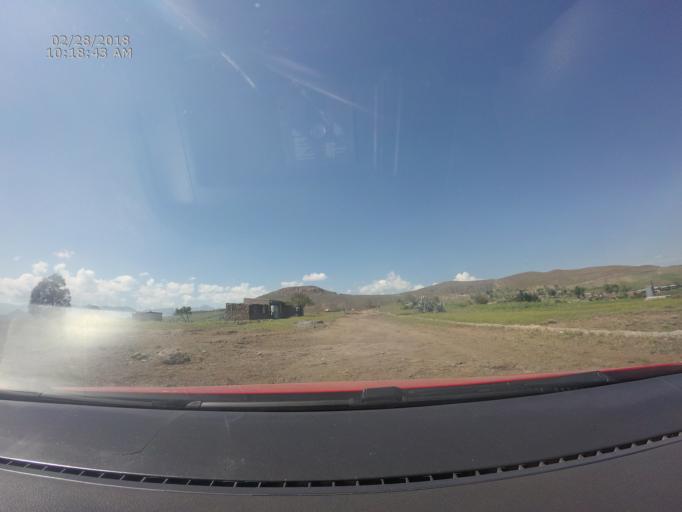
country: LS
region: Berea
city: Teyateyaneng
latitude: -29.2245
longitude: 27.8695
